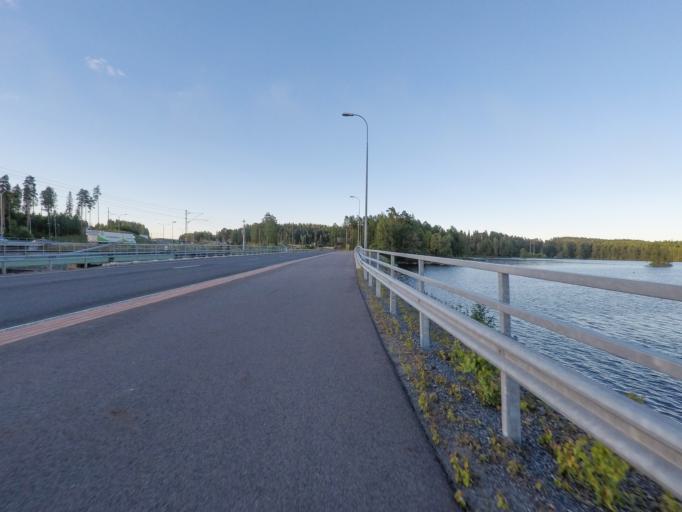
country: FI
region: Northern Savo
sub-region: Kuopio
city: Kuopio
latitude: 62.9533
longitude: 27.6840
